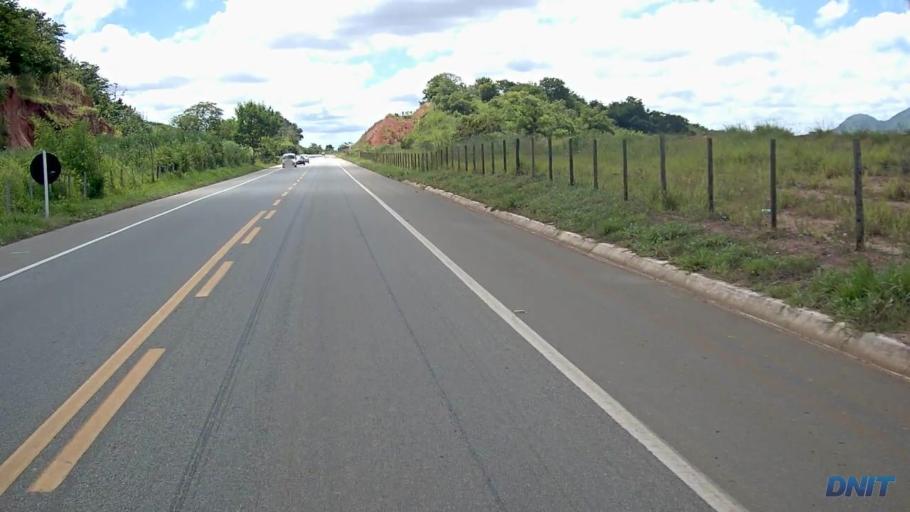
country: BR
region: Minas Gerais
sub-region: Governador Valadares
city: Governador Valadares
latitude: -18.9108
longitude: -42.0075
